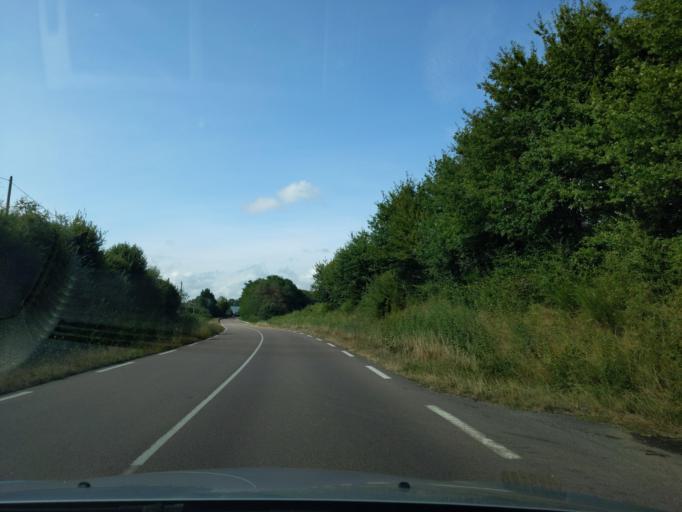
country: FR
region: Bourgogne
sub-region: Departement de Saone-et-Loire
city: Etang-sur-Arroux
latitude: 46.8761
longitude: 4.1354
